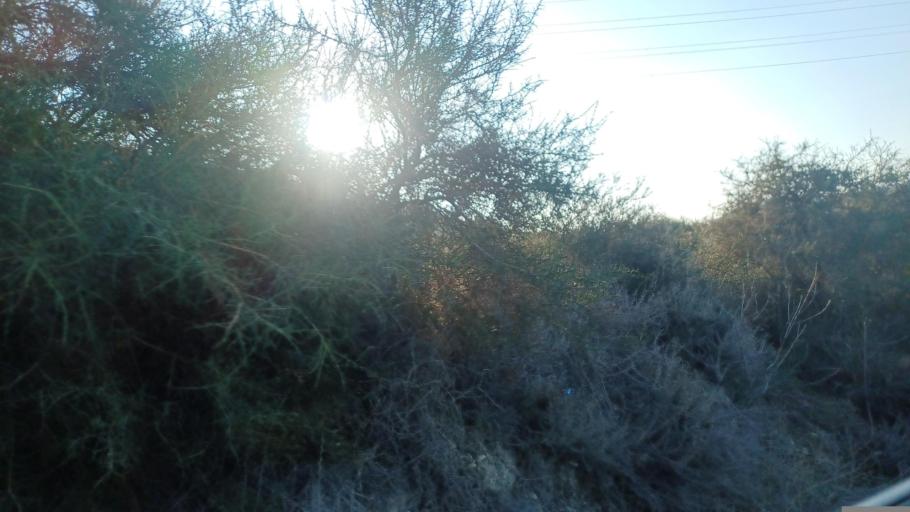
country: CY
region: Larnaka
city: Kofinou
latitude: 34.8257
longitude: 33.3088
